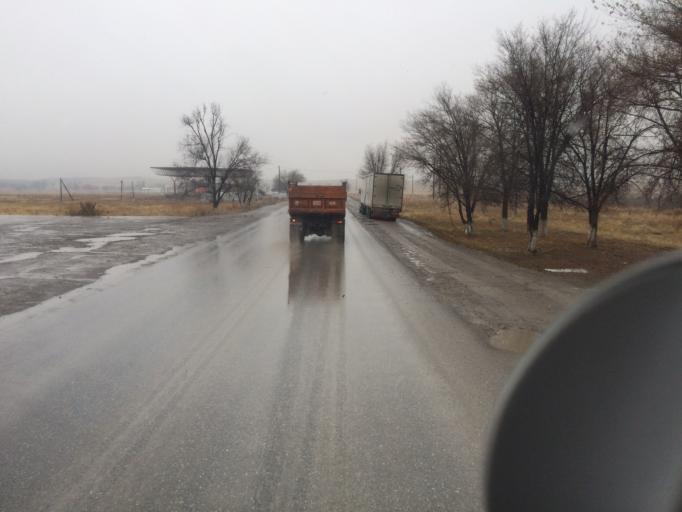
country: KG
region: Chuy
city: Kant
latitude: 43.0021
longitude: 74.8655
